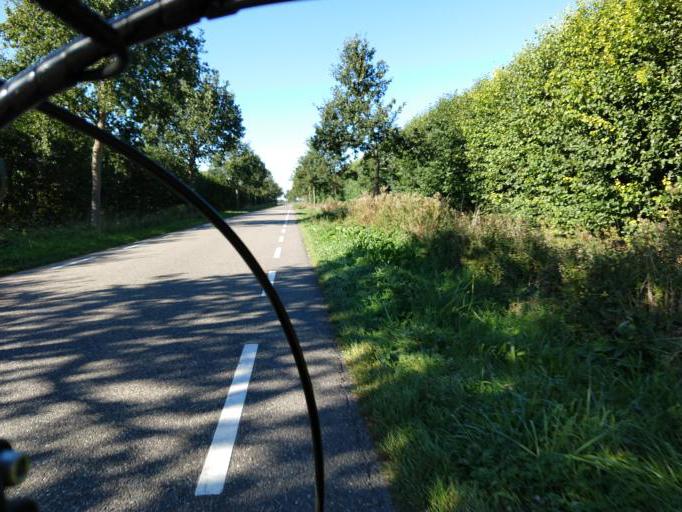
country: NL
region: Zeeland
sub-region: Gemeente Terneuzen
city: Terneuzen
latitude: 51.4182
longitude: 3.8379
